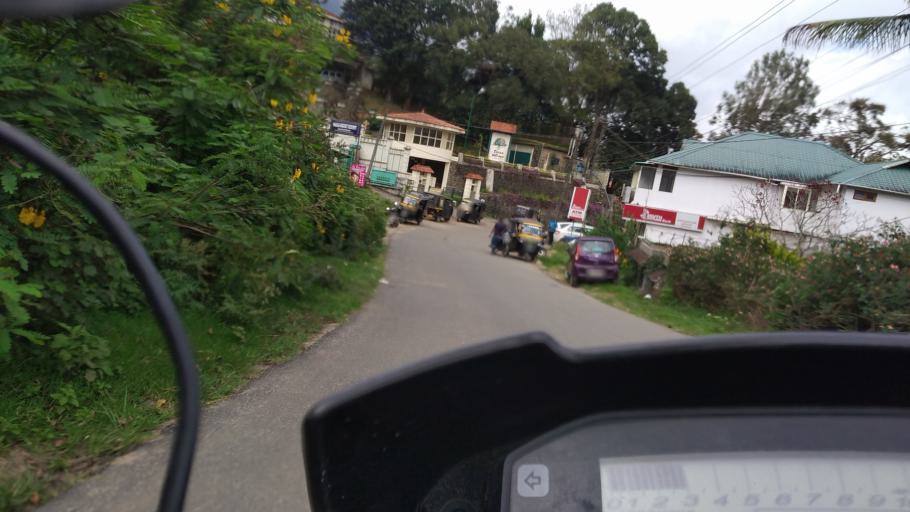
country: IN
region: Kerala
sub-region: Idukki
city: Munnar
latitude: 10.0413
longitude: 77.1773
